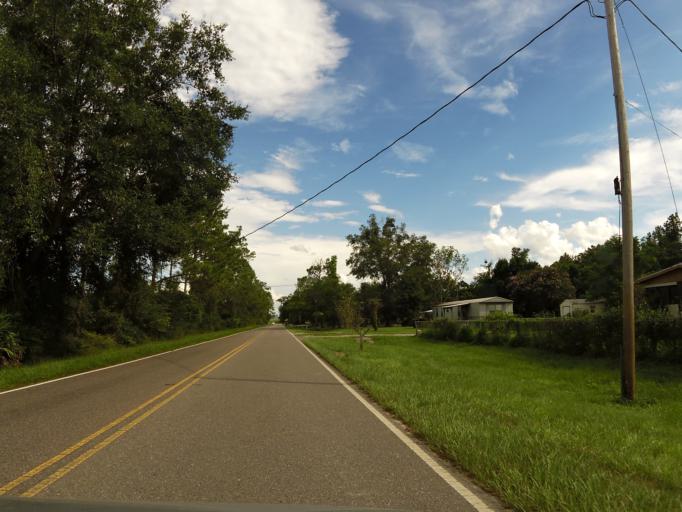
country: US
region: Florida
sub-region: Clay County
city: Green Cove Springs
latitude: 29.9374
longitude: -81.6905
